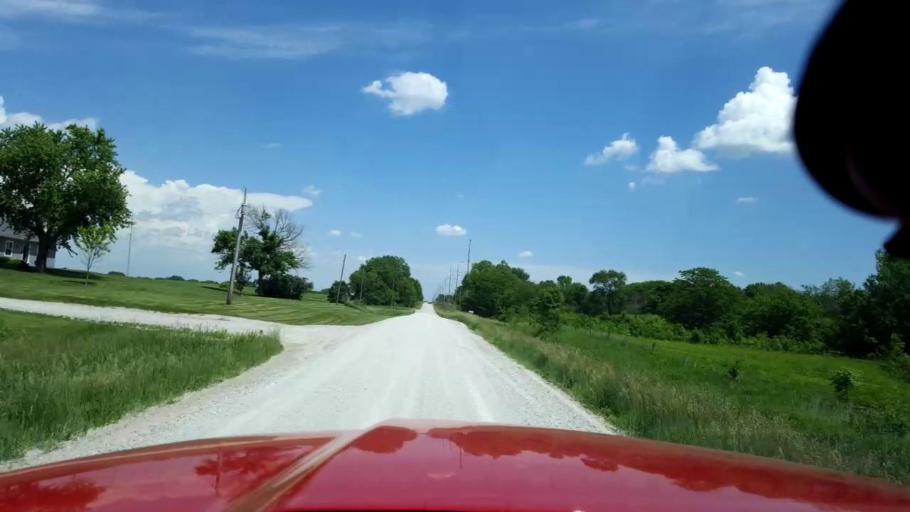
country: US
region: Iowa
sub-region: Boone County
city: Boone
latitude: 42.0492
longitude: -93.7601
